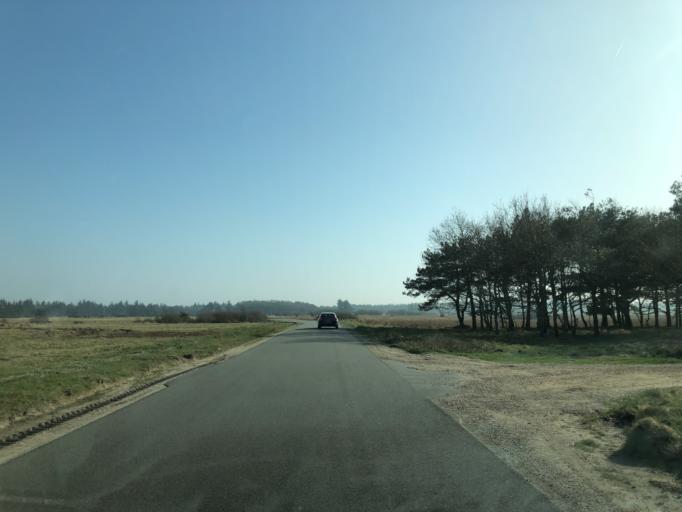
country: DK
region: South Denmark
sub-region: Varde Kommune
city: Oksbol
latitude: 55.6249
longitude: 8.1693
